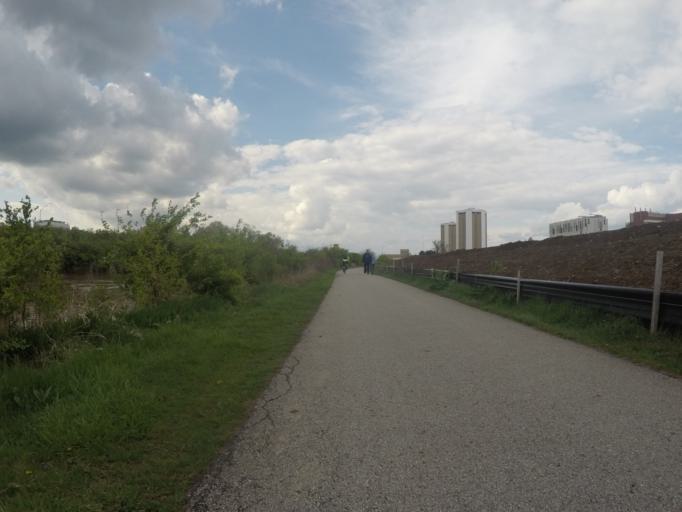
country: US
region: Ohio
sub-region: Franklin County
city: Grandview Heights
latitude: 39.9936
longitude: -83.0236
